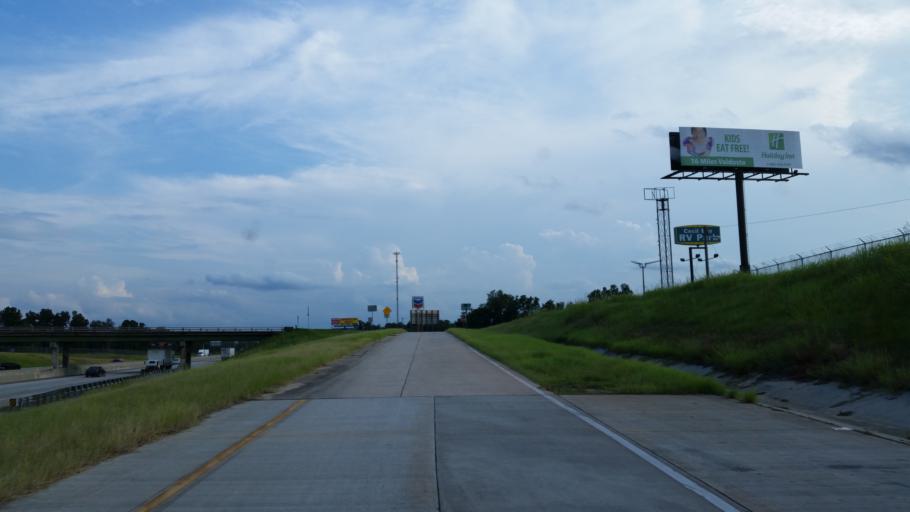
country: US
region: Georgia
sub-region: Lowndes County
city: Hahira
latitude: 31.0455
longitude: -83.3978
